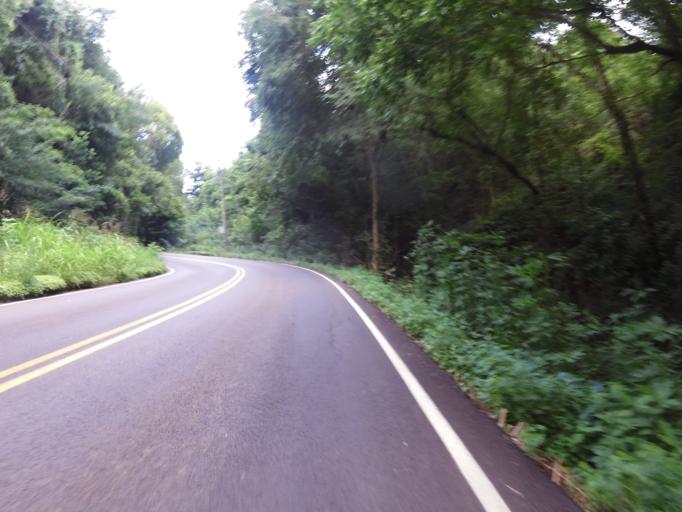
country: US
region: Tennessee
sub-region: Knox County
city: Knoxville
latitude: 35.9703
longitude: -83.8770
